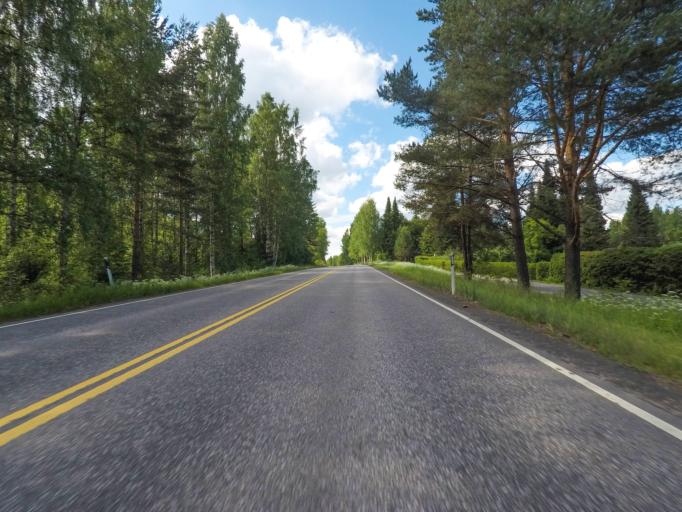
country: FI
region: Southern Savonia
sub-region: Savonlinna
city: Kerimaeki
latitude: 61.8222
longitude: 29.2506
